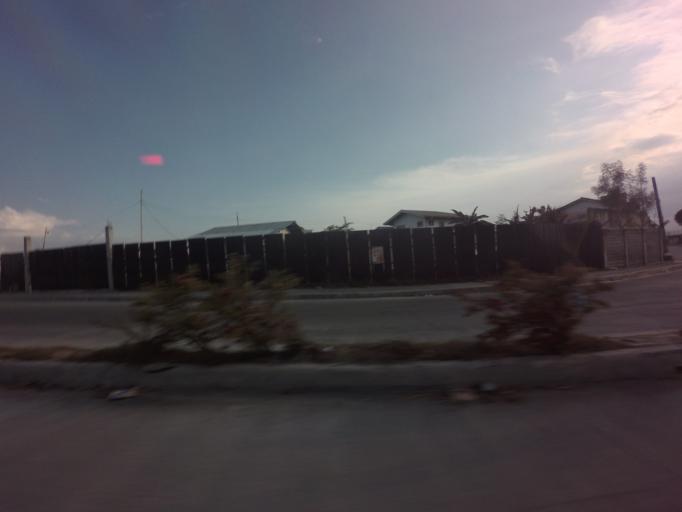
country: PH
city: Sambayanihan People's Village
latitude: 14.5029
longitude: 121.0129
